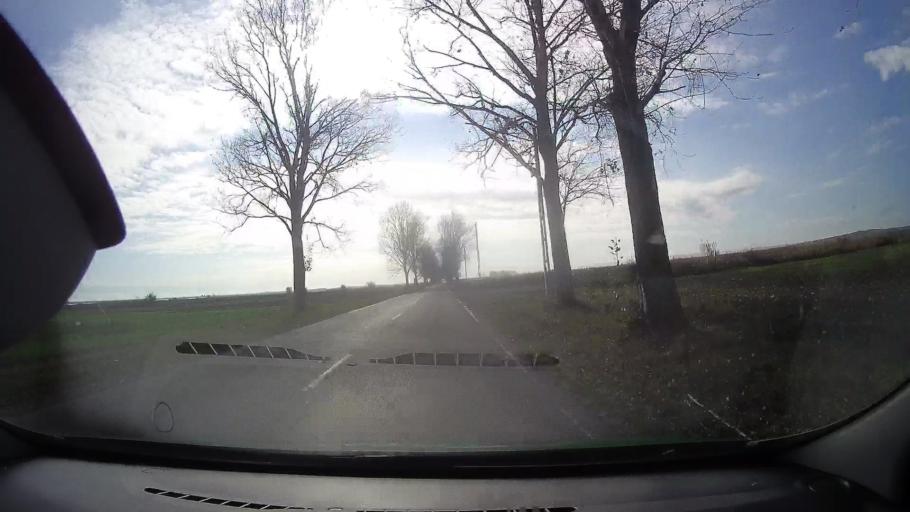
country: RO
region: Tulcea
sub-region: Comuna Valea Nucarilor
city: Agighiol
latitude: 45.0084
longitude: 28.8847
